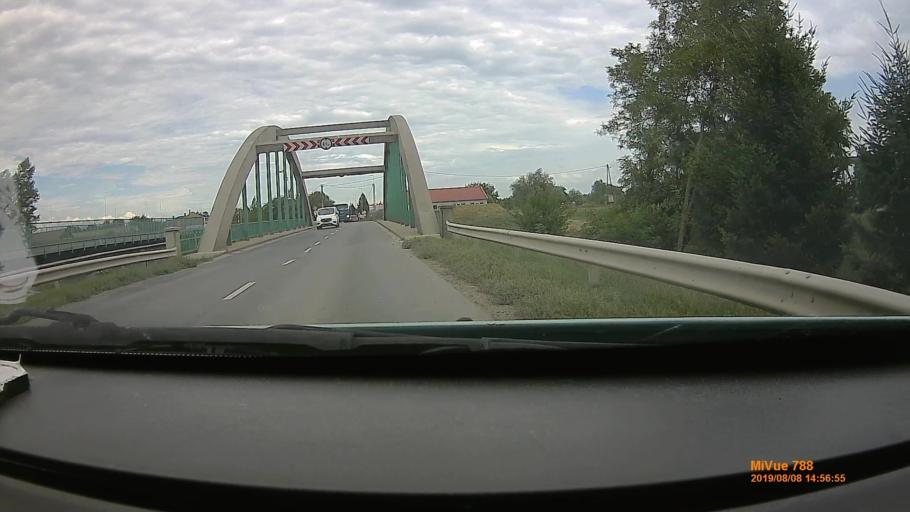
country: HU
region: Szabolcs-Szatmar-Bereg
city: Kocsord
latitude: 47.9422
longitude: 22.3576
